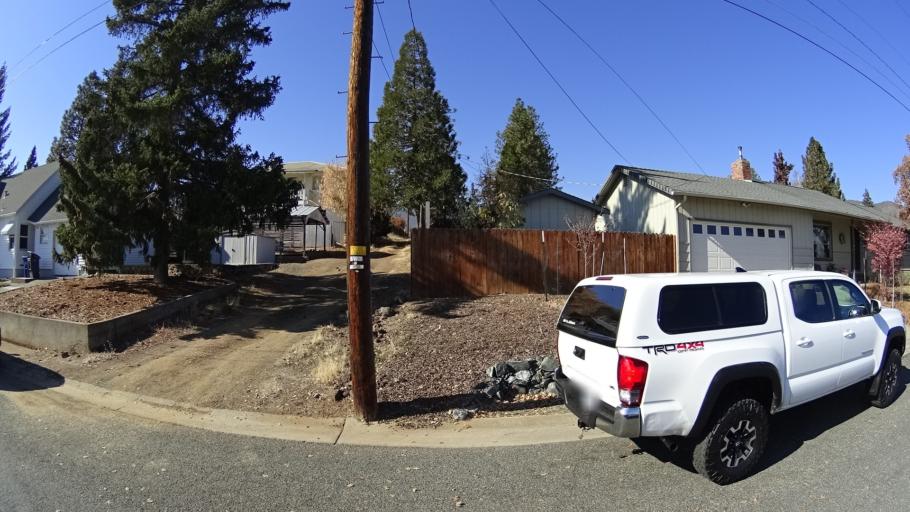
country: US
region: California
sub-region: Siskiyou County
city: Yreka
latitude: 41.7364
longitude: -122.6423
